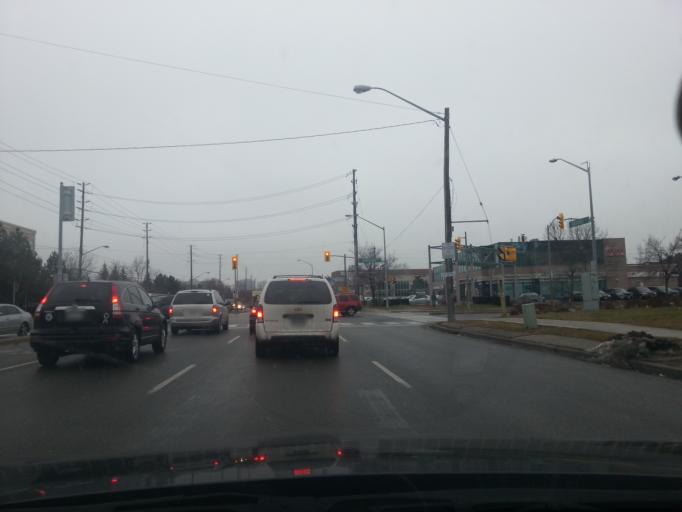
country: CA
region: Ontario
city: Concord
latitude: 43.7940
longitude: -79.4460
